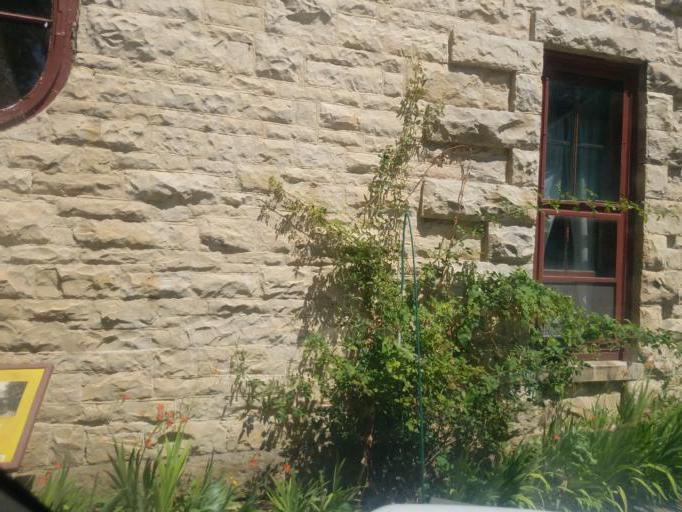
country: US
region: Ohio
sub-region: Logan County
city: West Liberty
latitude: 40.2510
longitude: -83.7268
